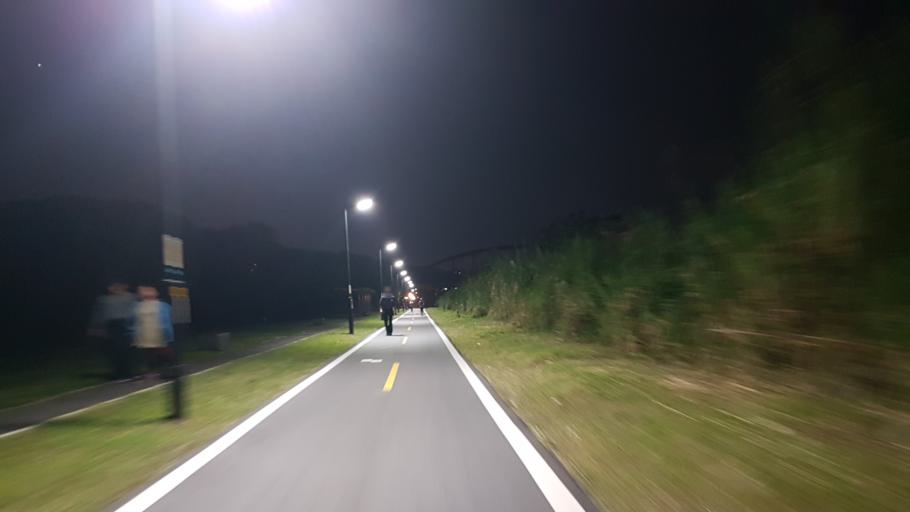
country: TW
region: Taipei
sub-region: Taipei
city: Banqiao
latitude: 24.9725
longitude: 121.5248
